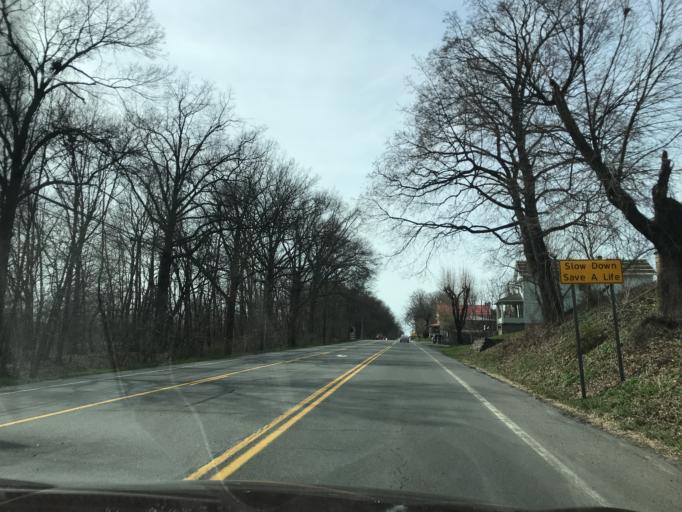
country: US
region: Pennsylvania
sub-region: Northumberland County
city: Northumberland
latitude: 40.8953
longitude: -76.8114
